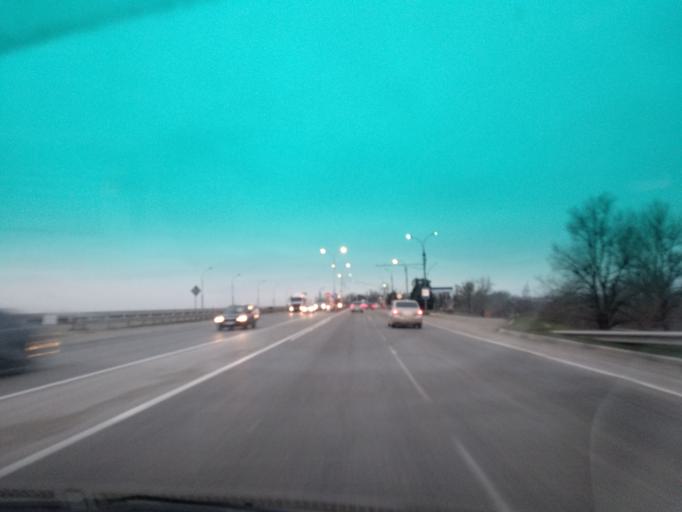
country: RU
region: Krasnodarskiy
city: Pashkovskiy
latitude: 45.0008
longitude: 39.1152
